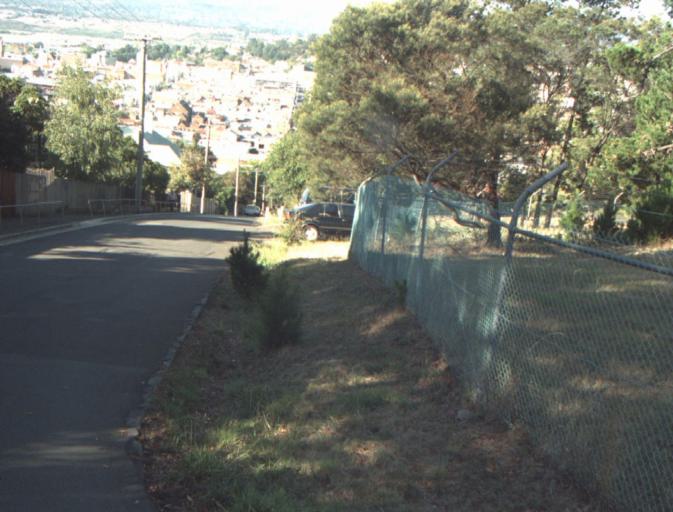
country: AU
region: Tasmania
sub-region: Launceston
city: West Launceston
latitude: -41.4444
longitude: 147.1291
